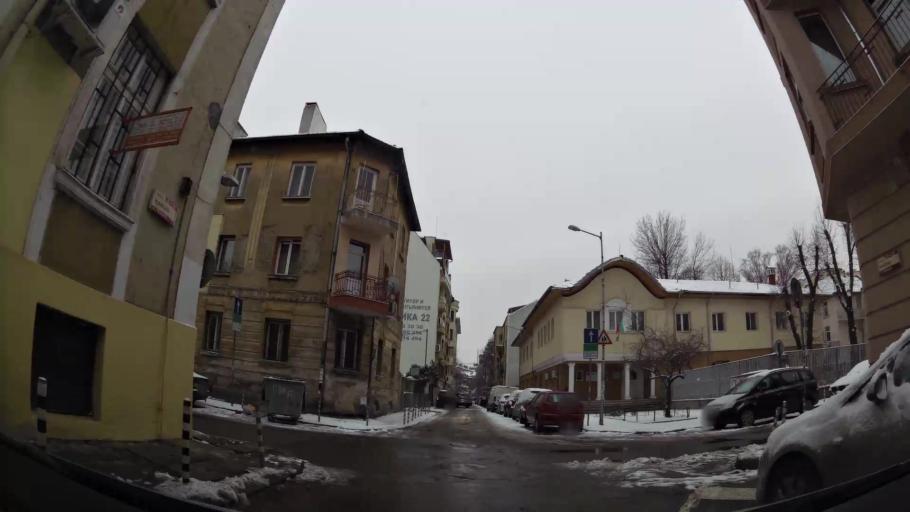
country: BG
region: Sofia-Capital
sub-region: Stolichna Obshtina
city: Sofia
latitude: 42.7027
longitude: 23.3319
